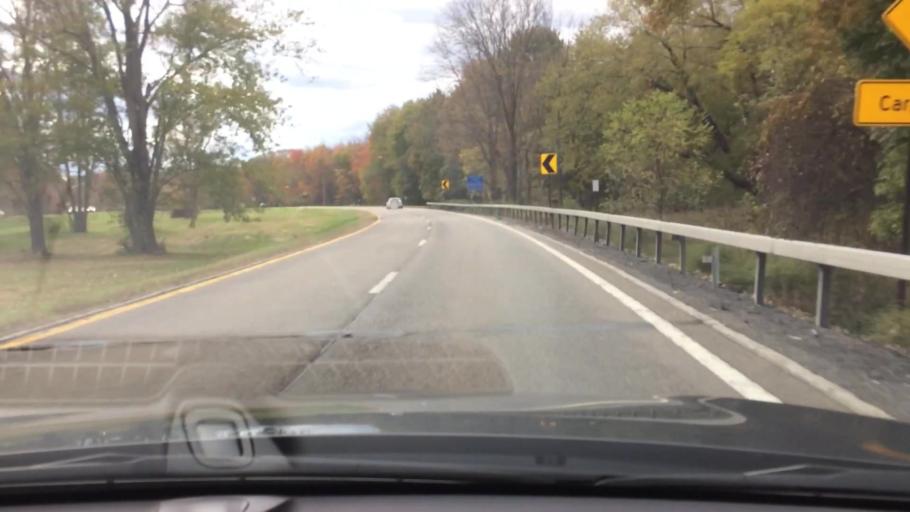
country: US
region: New York
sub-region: Dutchess County
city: Hillside Lake
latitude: 41.5826
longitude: -73.7758
